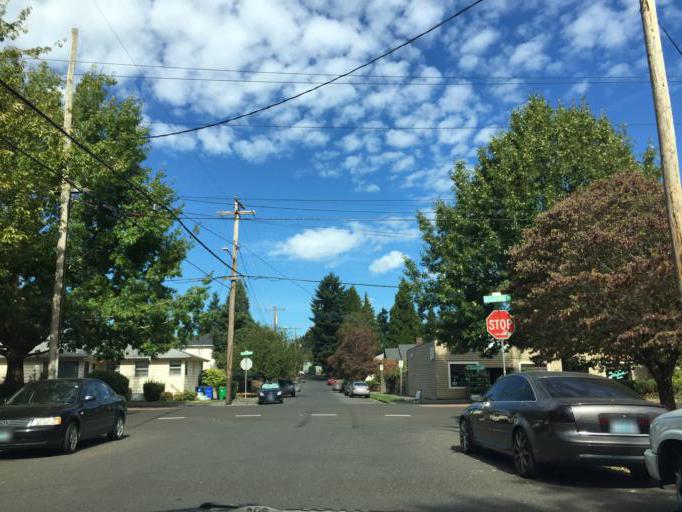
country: US
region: Oregon
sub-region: Clackamas County
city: Milwaukie
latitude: 45.4930
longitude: -122.6246
